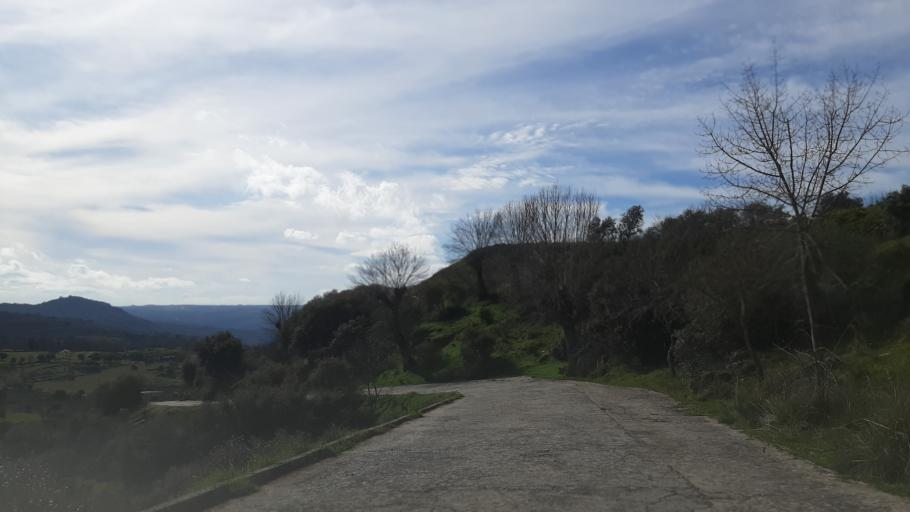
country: ES
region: Castille and Leon
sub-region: Provincia de Salamanca
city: Villarino de los Aires
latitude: 41.2621
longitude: -6.5269
